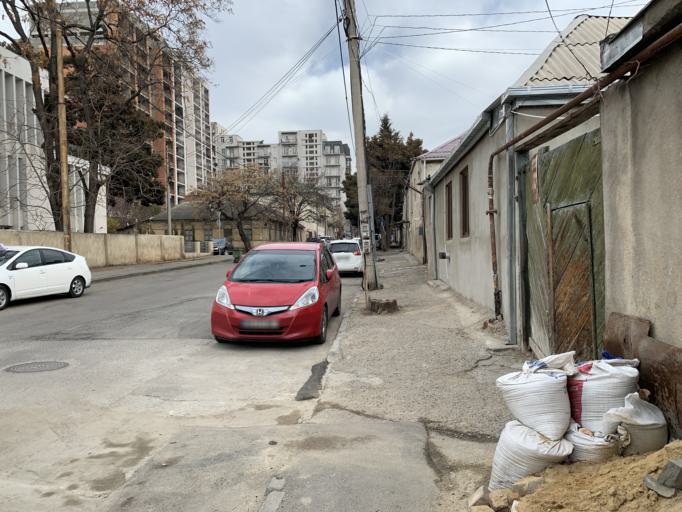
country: GE
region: T'bilisi
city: Tbilisi
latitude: 41.6792
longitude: 44.8392
